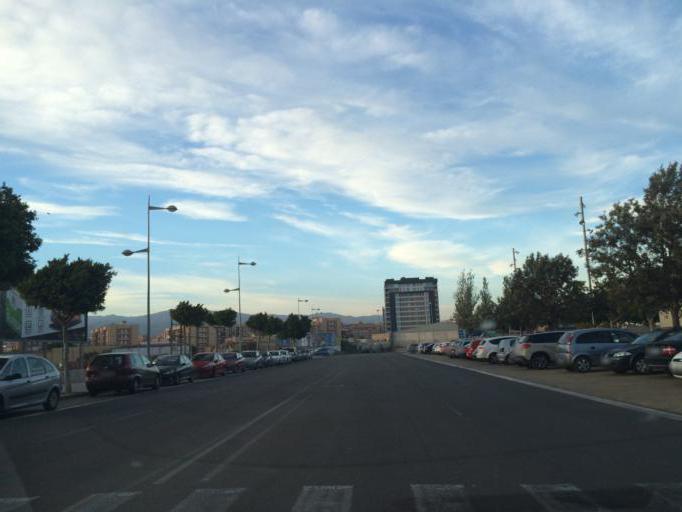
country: ES
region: Andalusia
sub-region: Provincia de Almeria
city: Almeria
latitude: 36.8380
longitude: -2.4392
